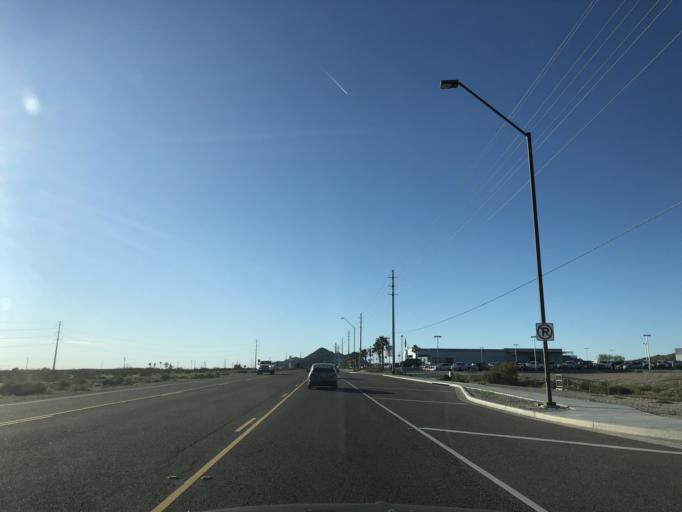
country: US
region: Arizona
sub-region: Maricopa County
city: Buckeye
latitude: 33.4355
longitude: -112.5775
